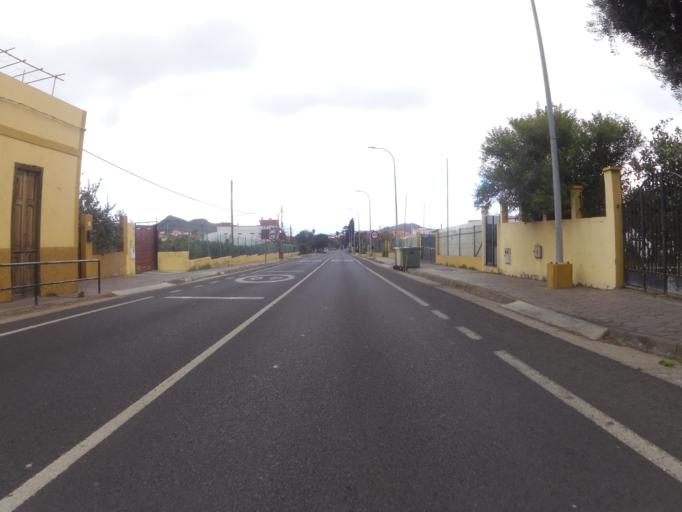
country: ES
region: Canary Islands
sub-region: Provincia de Las Palmas
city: Valsequillo de Gran Canaria
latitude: 27.9933
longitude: -15.4842
